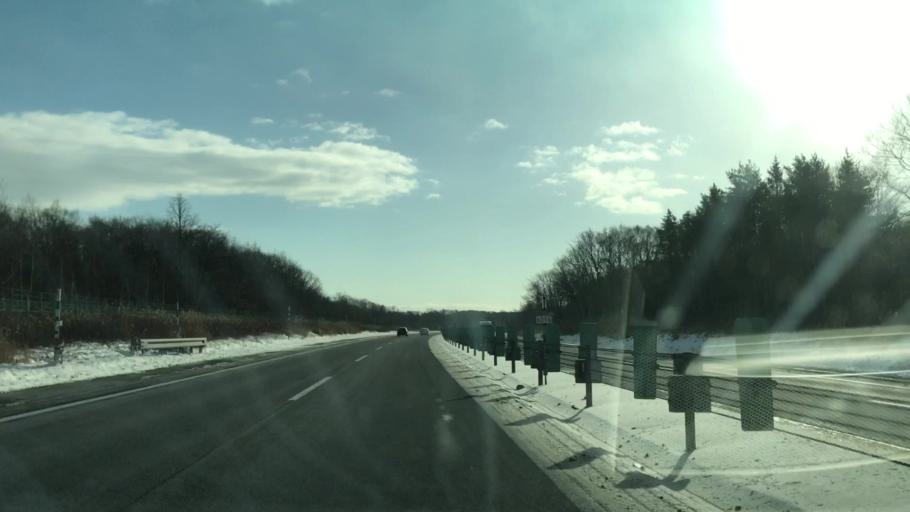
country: JP
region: Hokkaido
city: Chitose
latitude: 42.8388
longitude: 141.6021
